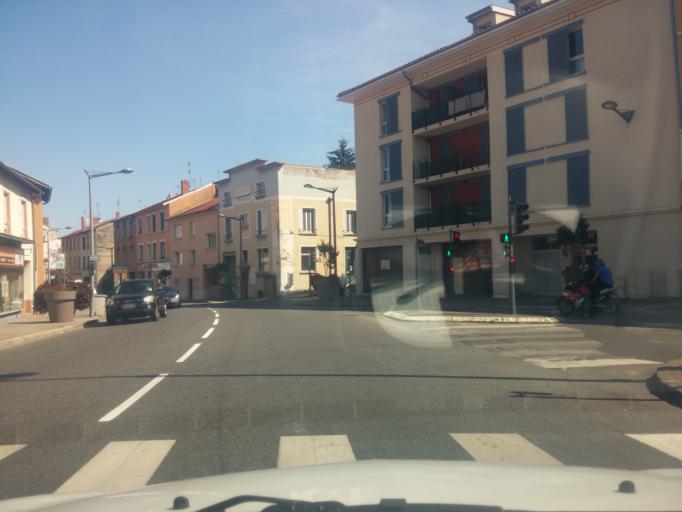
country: FR
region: Rhone-Alpes
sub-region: Departement du Rhone
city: Oullins
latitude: 45.7200
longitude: 4.7983
